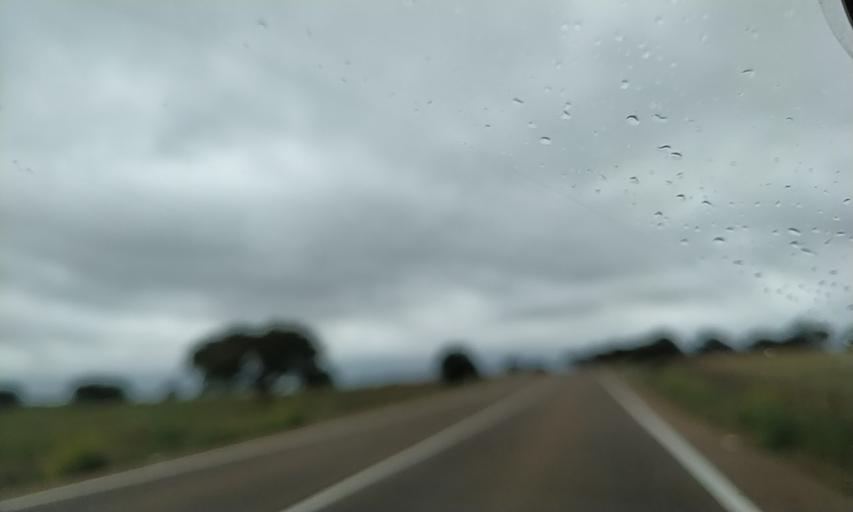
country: ES
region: Extremadura
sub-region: Provincia de Badajoz
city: Villar del Rey
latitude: 39.0277
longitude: -6.8388
